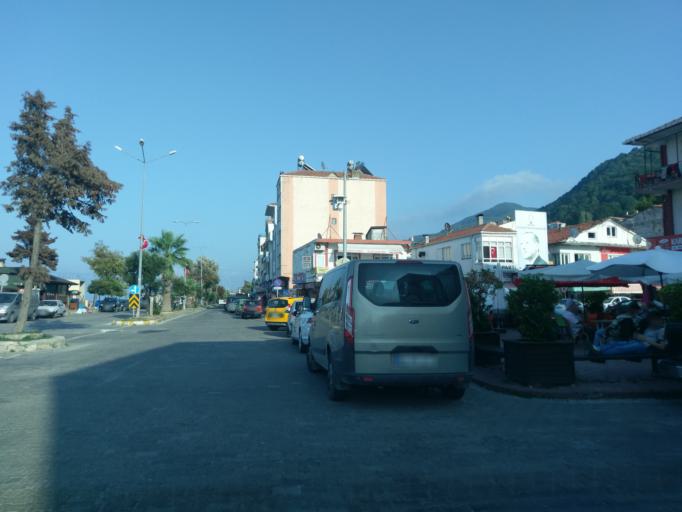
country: TR
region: Kastamonu
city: Catalzeytin
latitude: 41.9542
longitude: 34.2133
